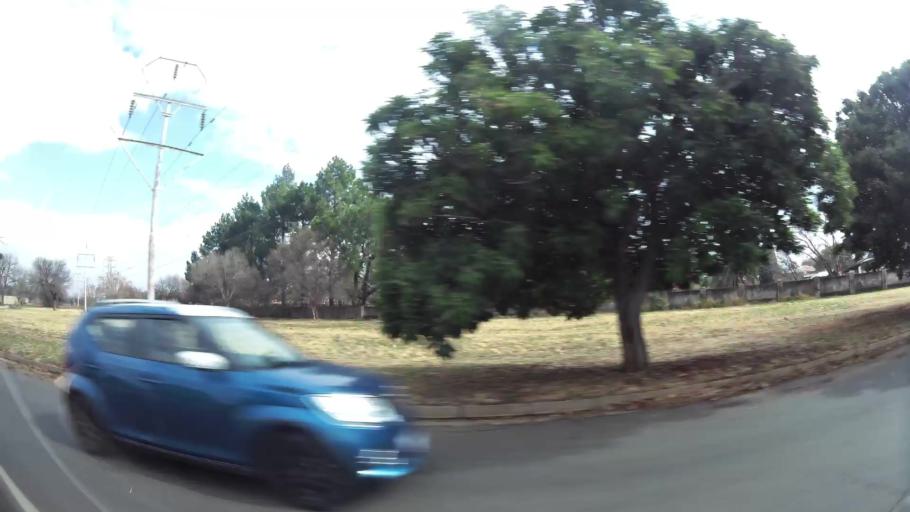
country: ZA
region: Gauteng
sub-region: Sedibeng District Municipality
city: Vereeniging
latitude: -26.6504
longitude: 27.9686
